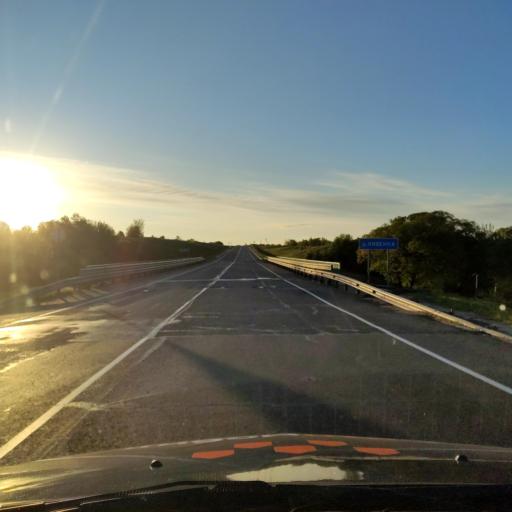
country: RU
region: Orjol
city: Livny
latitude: 52.4494
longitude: 37.6130
